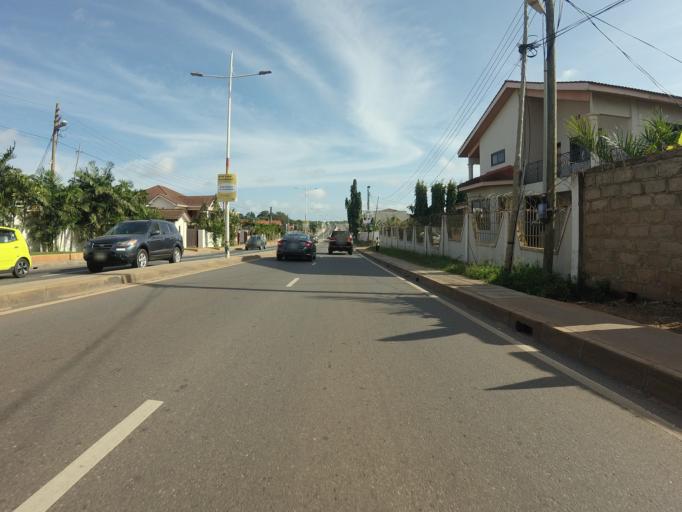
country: GH
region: Greater Accra
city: Medina Estates
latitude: 5.6225
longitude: -0.1528
